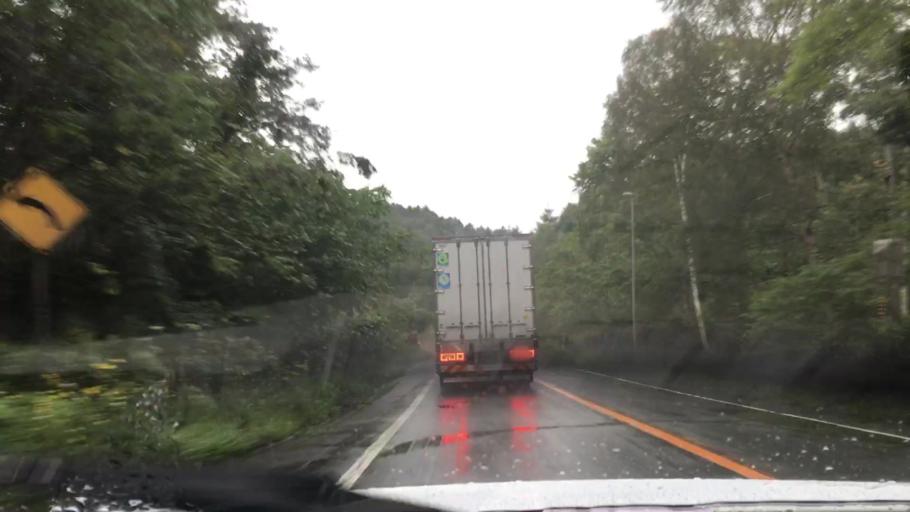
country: JP
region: Hokkaido
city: Niseko Town
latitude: 42.5961
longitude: 140.6738
